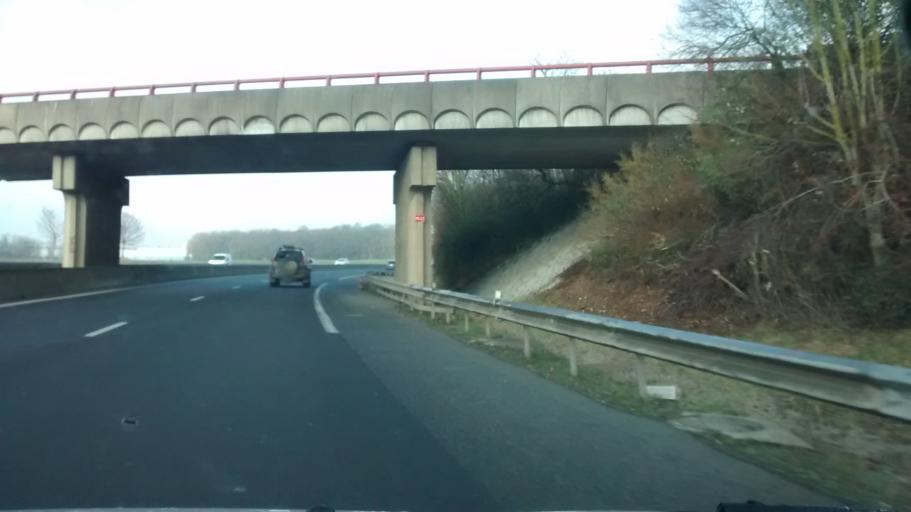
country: FR
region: Centre
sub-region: Departement d'Indre-et-Loire
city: Joue-les-Tours
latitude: 47.3312
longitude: 0.6755
